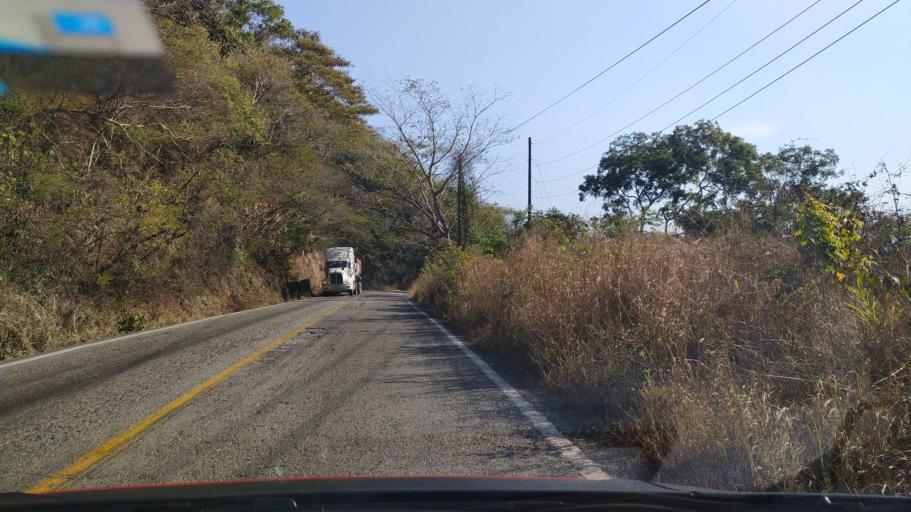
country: MX
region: Michoacan
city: Coahuayana Viejo
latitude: 18.6027
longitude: -103.6795
